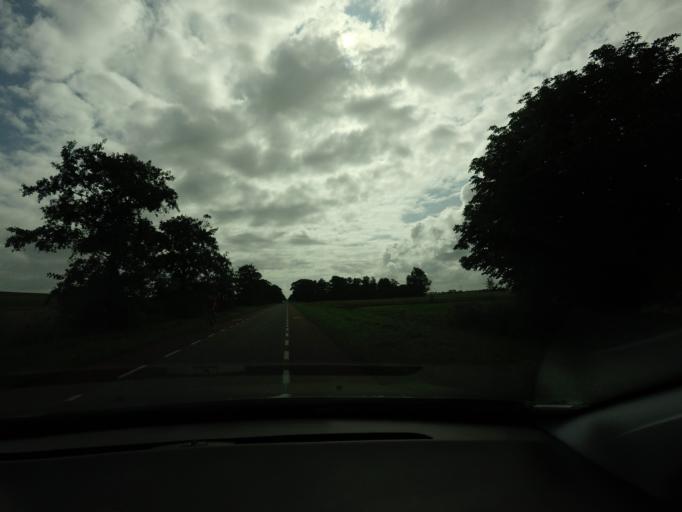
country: NL
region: North Holland
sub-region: Gemeente Hollands Kroon
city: Den Oever
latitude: 52.8744
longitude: 5.0886
